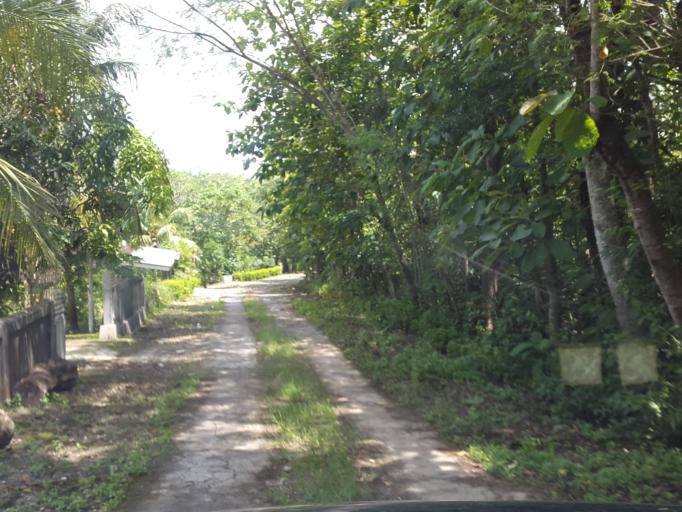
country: ID
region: Daerah Istimewa Yogyakarta
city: Wonosari
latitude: -7.9481
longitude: 110.6519
